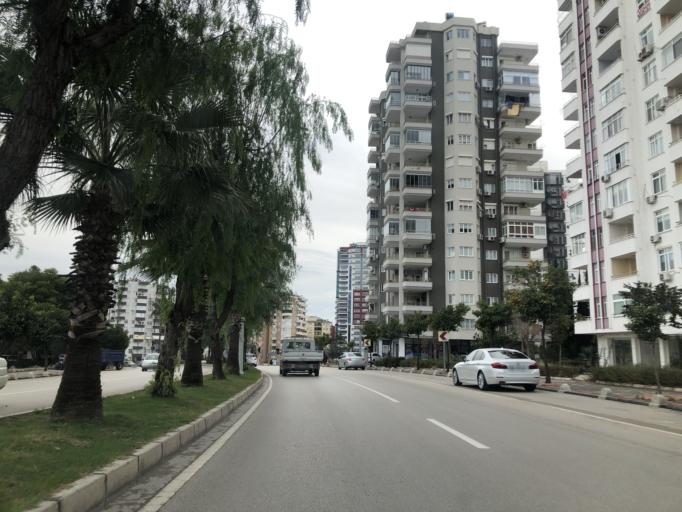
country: TR
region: Adana
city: Adana
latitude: 37.0552
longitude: 35.2872
